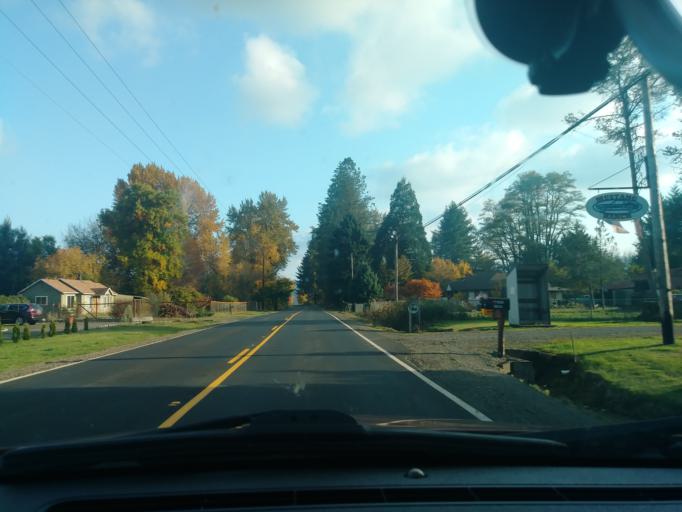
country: US
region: Oregon
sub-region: Washington County
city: Banks
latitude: 45.6031
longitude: -123.2285
